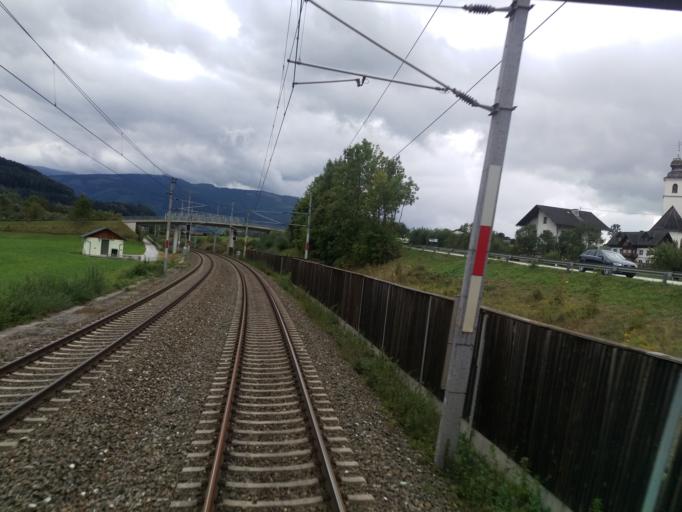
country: AT
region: Styria
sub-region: Politischer Bezirk Liezen
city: Stainach
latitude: 47.5399
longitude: 14.1194
